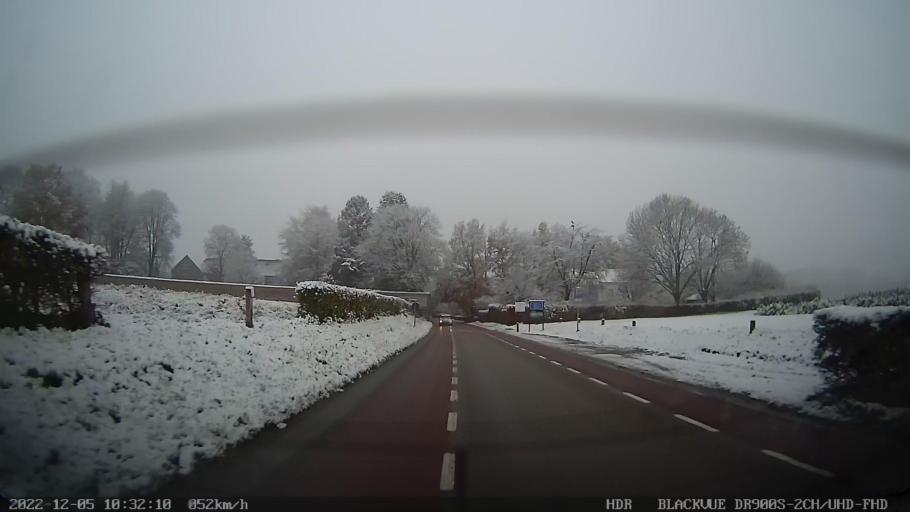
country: NL
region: Limburg
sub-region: Gemeente Voerendaal
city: Ubachsberg
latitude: 50.8149
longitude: 5.9151
